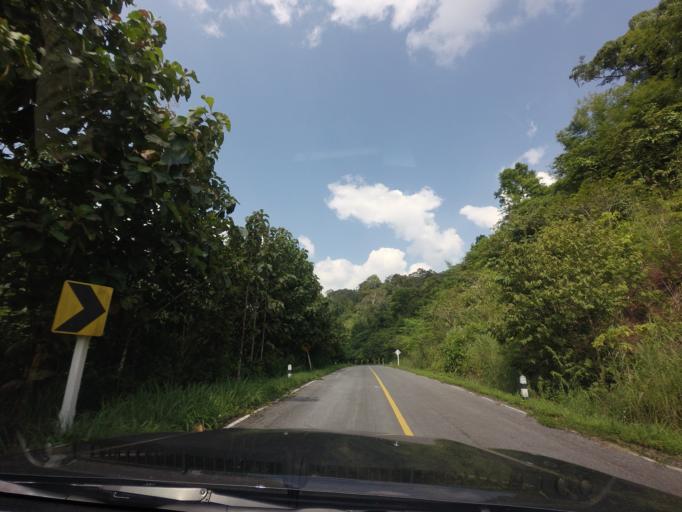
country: TH
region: Uttaradit
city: Ban Khok
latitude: 18.1937
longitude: 101.0527
